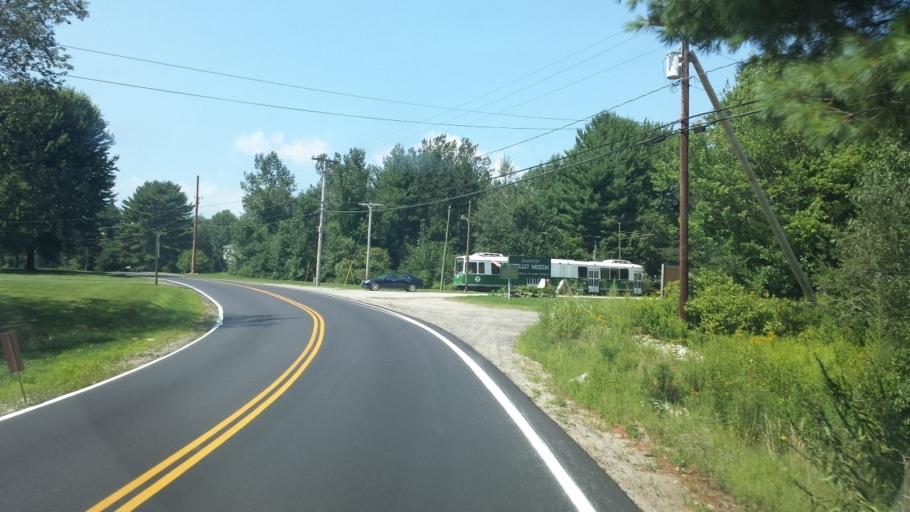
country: US
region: Maine
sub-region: York County
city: Arundel
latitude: 43.4068
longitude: -70.4894
